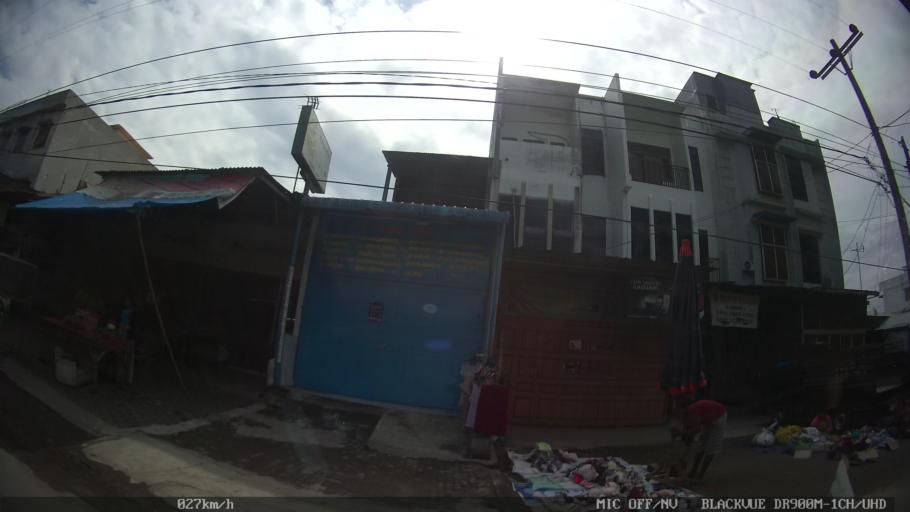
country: ID
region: North Sumatra
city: Sunggal
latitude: 3.6028
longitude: 98.6084
